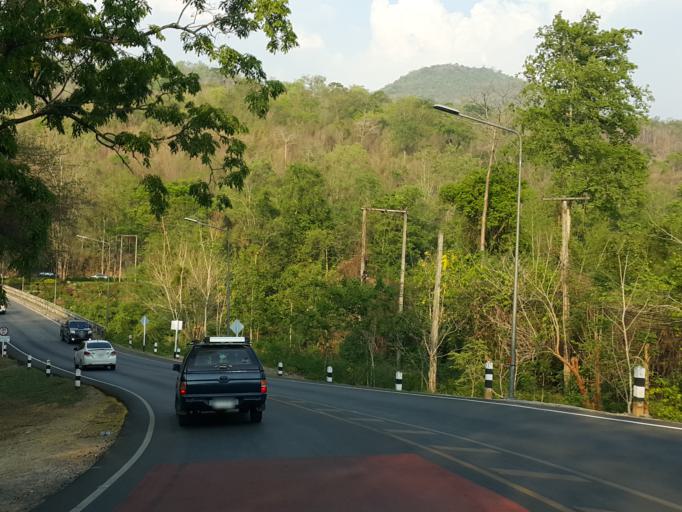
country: TH
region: Kanchanaburi
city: Si Sawat
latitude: 14.3852
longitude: 99.1422
